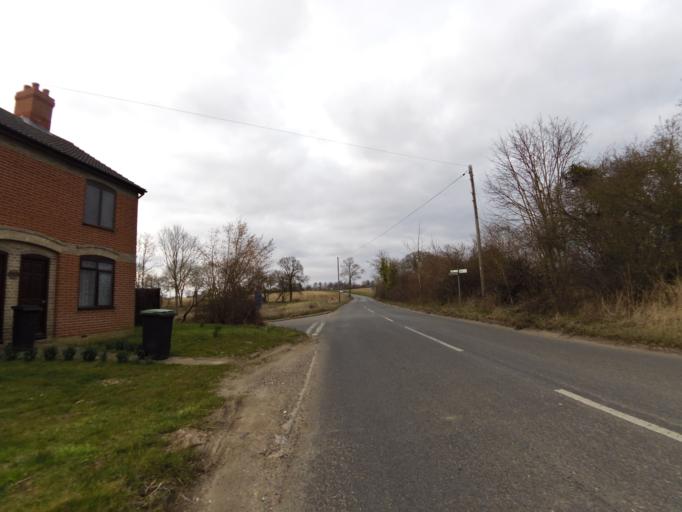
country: GB
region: England
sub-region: Suffolk
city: Ipswich
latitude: 52.1102
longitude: 1.1522
